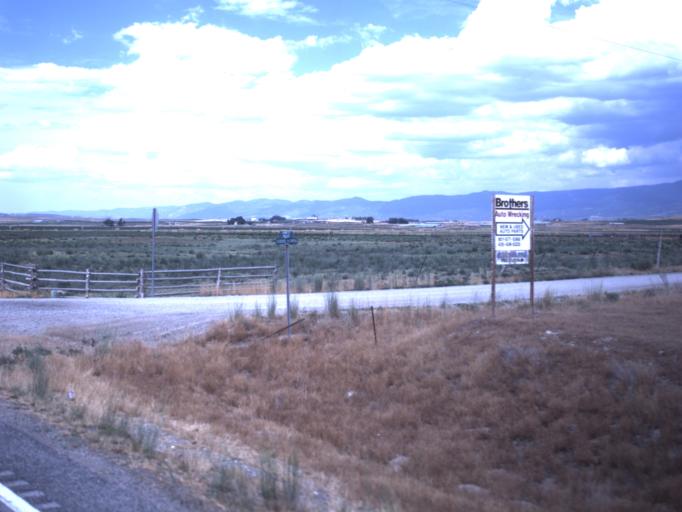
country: US
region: Utah
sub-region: Sanpete County
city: Moroni
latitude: 39.4613
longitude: -111.5626
